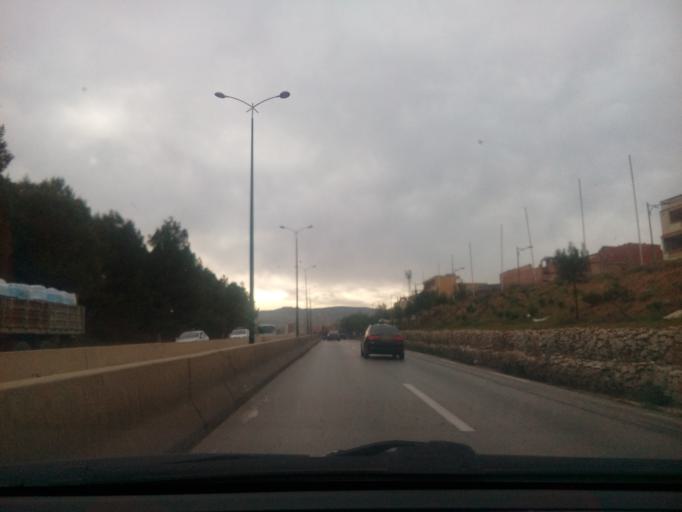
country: DZ
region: Tlemcen
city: Mansoura
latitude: 34.8900
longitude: -1.3553
